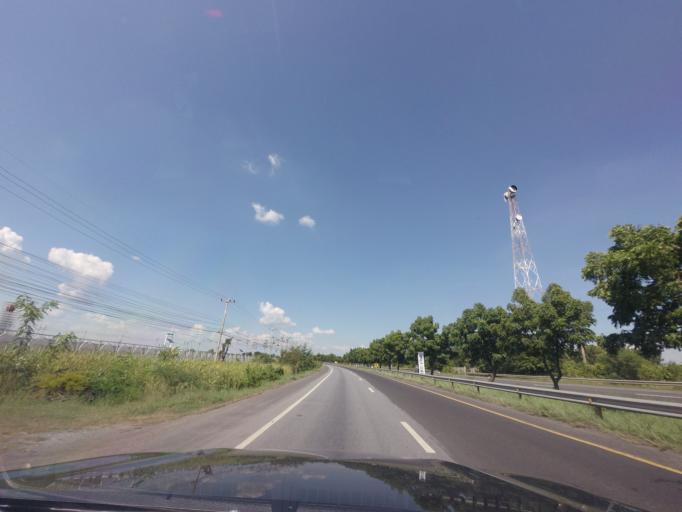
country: TH
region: Nakhon Ratchasima
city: Non Sung
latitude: 15.1901
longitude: 102.3463
